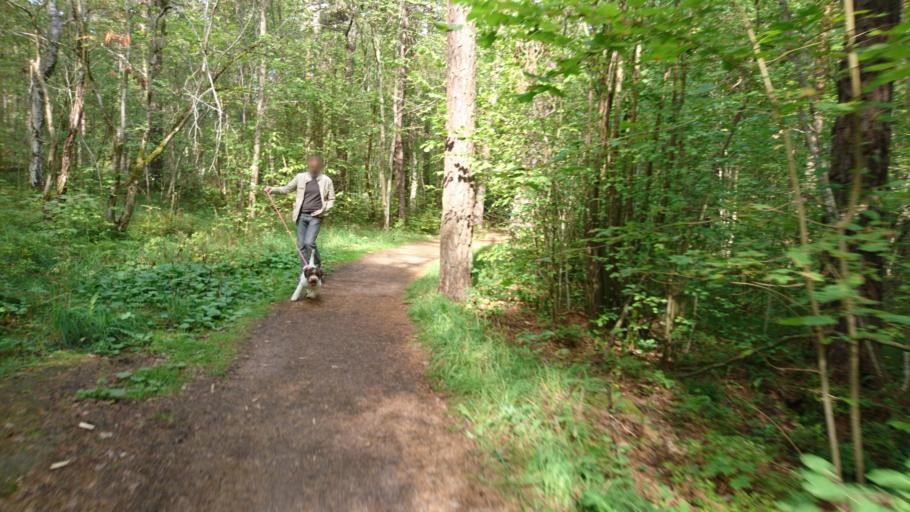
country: SE
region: Uppsala
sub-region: Uppsala Kommun
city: Uppsala
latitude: 59.8440
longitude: 17.6211
